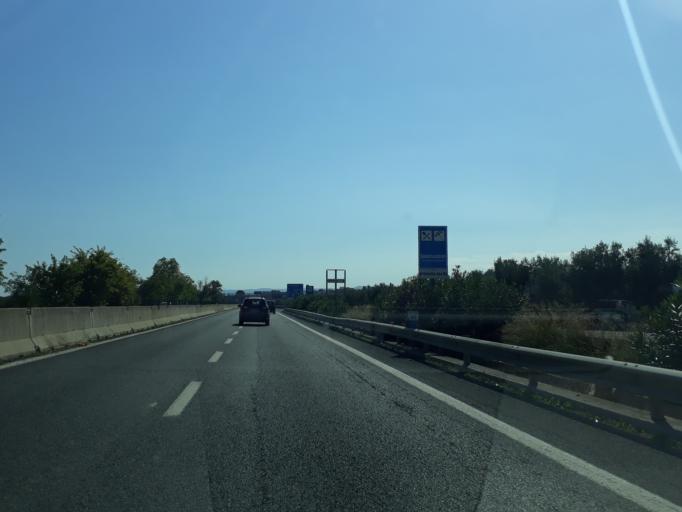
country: IT
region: Apulia
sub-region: Provincia di Bari
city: Monopoli
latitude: 40.8993
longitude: 17.3283
